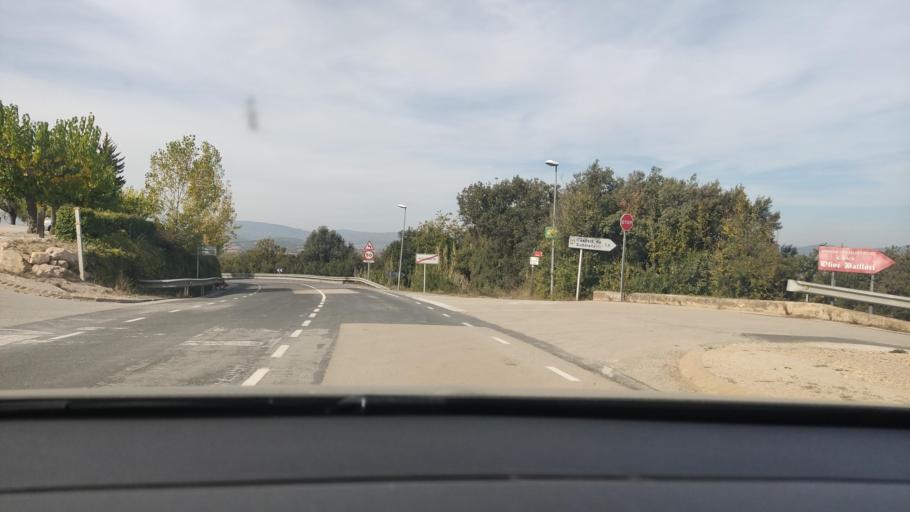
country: ES
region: Catalonia
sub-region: Provincia de Barcelona
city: Sant Sadurni d'Anoia
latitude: 41.4095
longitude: 1.8078
